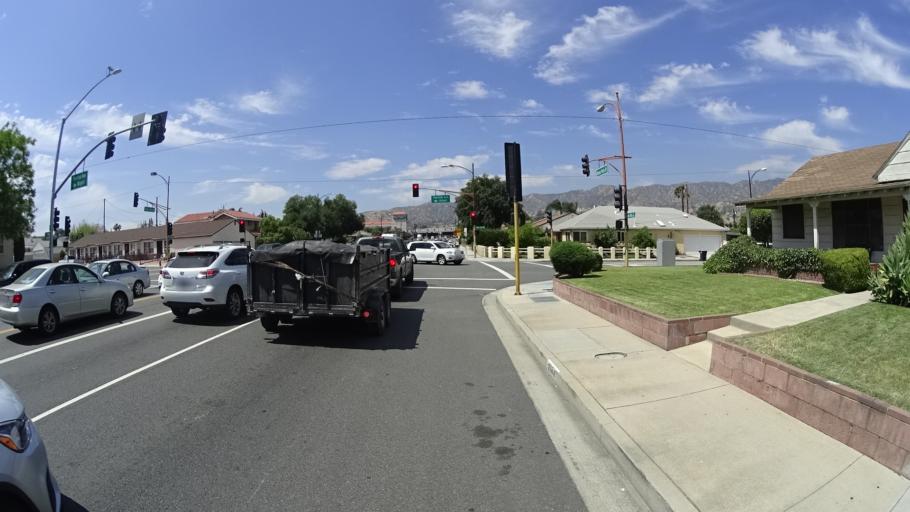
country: US
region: California
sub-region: Los Angeles County
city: Burbank
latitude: 34.1952
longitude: -118.3378
